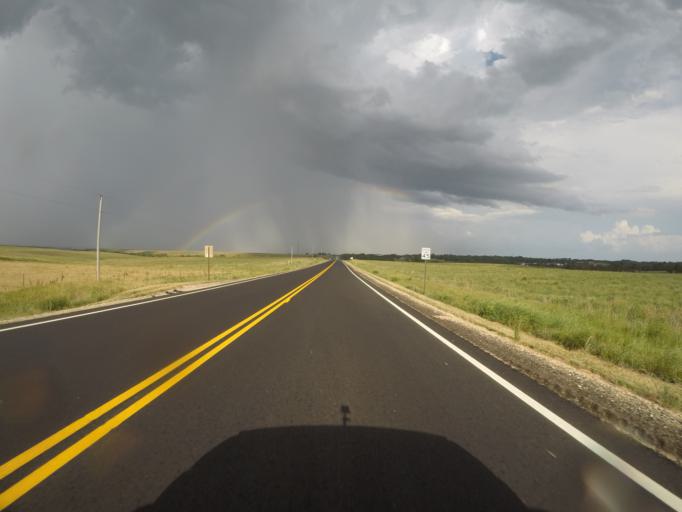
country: US
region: Kansas
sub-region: Marshall County
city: Blue Rapids
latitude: 39.4363
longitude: -96.7721
